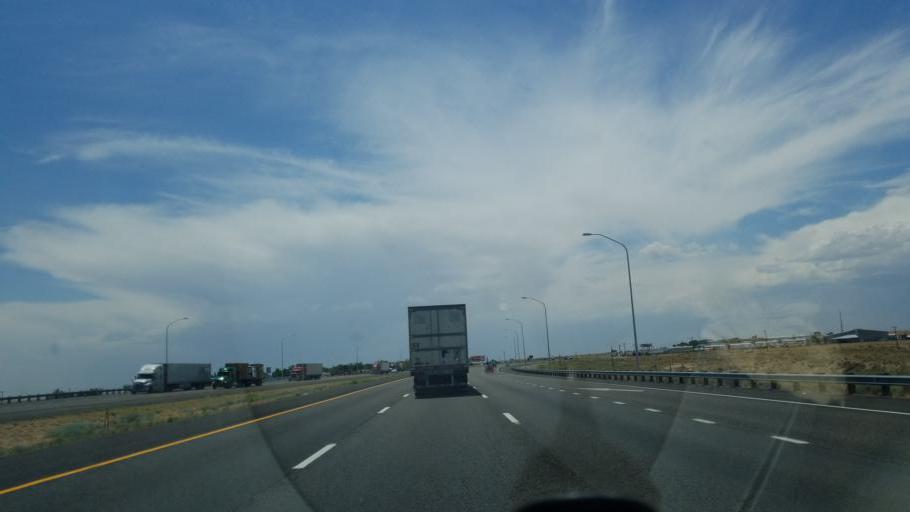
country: US
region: New Mexico
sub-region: Bernalillo County
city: South Valley
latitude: 35.0634
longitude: -106.7915
